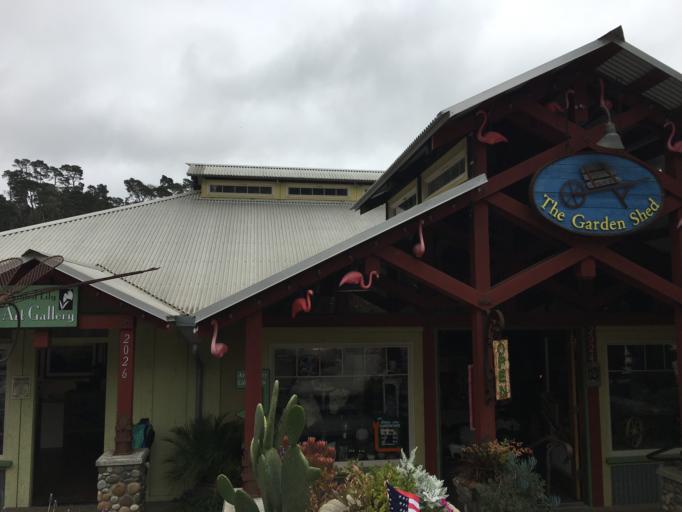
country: US
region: California
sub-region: San Luis Obispo County
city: Cambria
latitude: 35.5635
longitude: -121.0845
